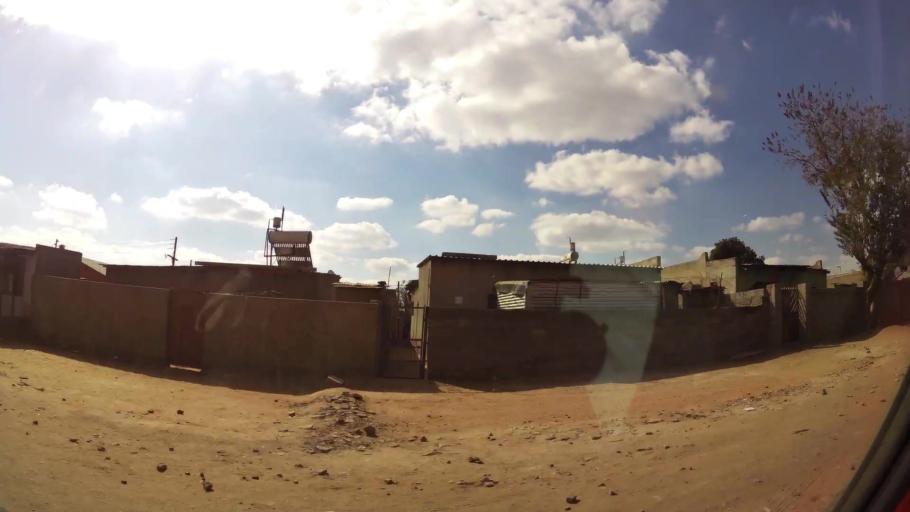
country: ZA
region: Gauteng
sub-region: Ekurhuleni Metropolitan Municipality
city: Tembisa
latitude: -25.9938
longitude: 28.2025
